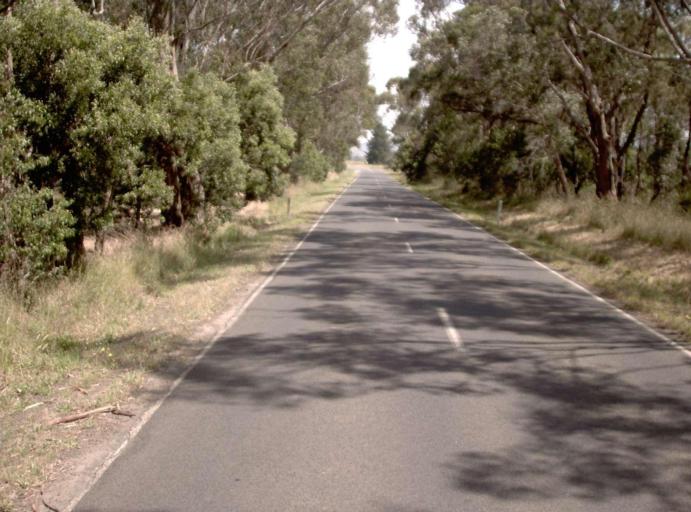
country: AU
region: Victoria
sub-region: Latrobe
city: Traralgon
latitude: -38.2623
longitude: 146.5465
